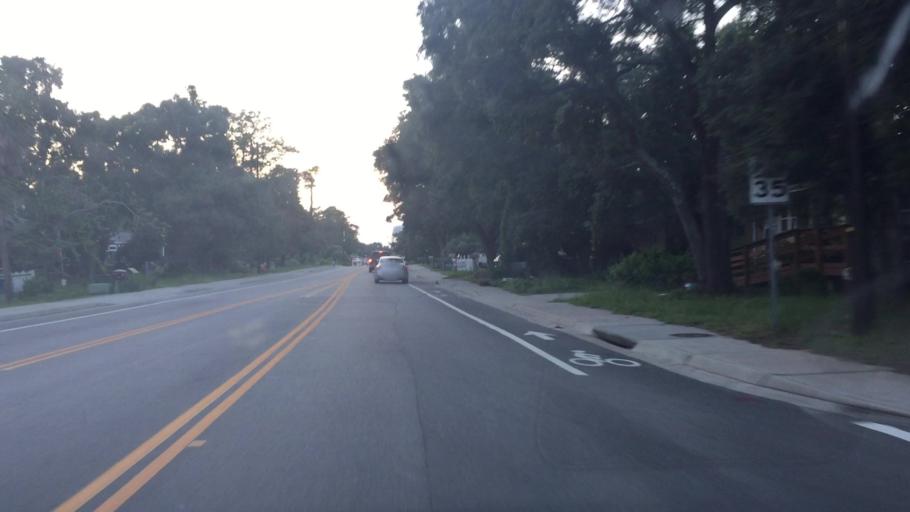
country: US
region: South Carolina
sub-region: Horry County
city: Myrtle Beach
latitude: 33.6858
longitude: -78.8928
